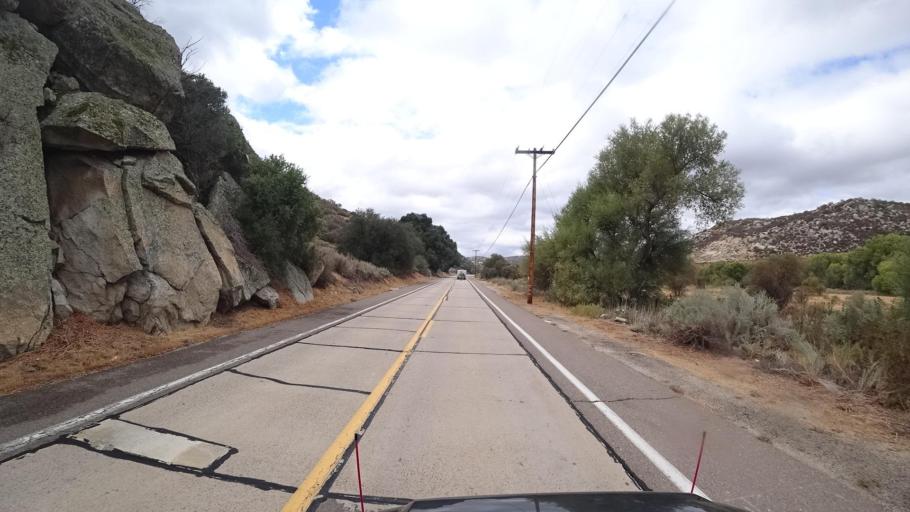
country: US
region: California
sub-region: San Diego County
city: Campo
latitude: 32.7234
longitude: -116.4362
